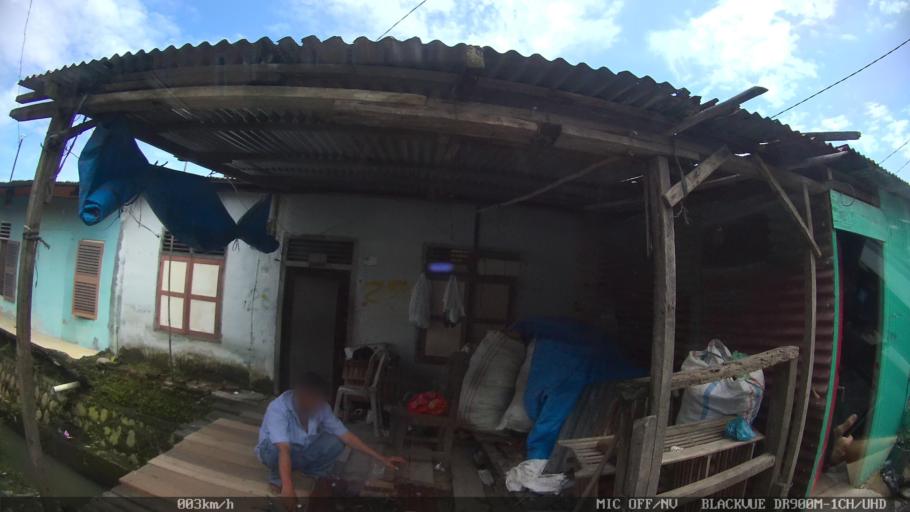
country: ID
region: North Sumatra
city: Medan
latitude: 3.5919
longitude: 98.7395
